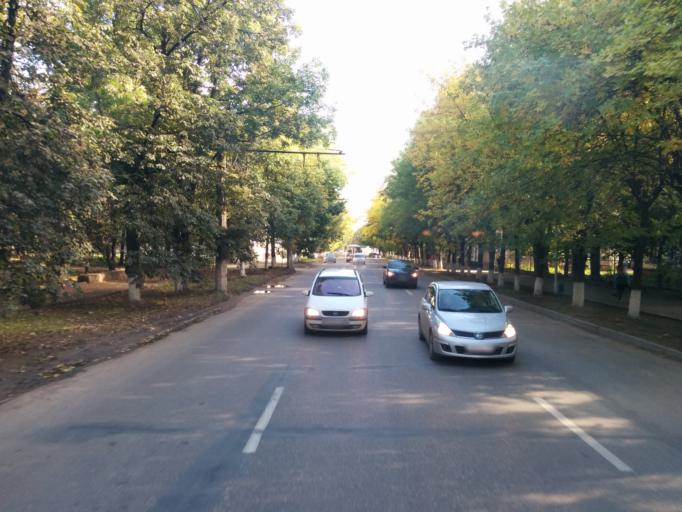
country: RU
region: Bashkortostan
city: Ufa
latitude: 54.8216
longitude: 56.0678
